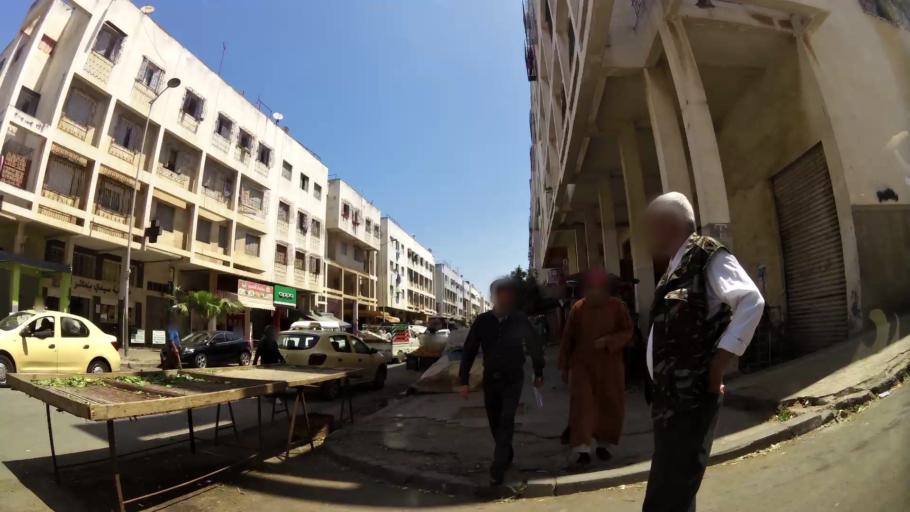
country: MA
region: Rabat-Sale-Zemmour-Zaer
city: Sale
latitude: 34.0668
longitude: -6.7882
